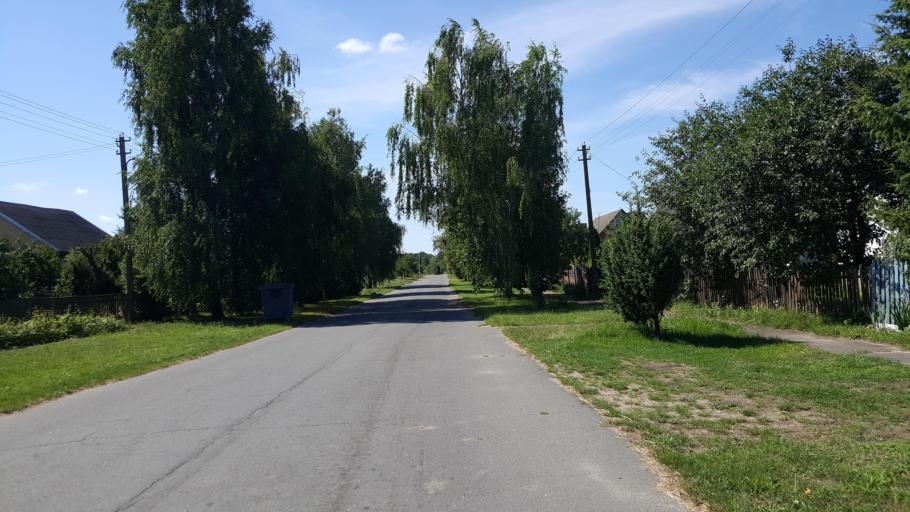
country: BY
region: Brest
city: Charnawchytsy
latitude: 52.2760
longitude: 23.7646
